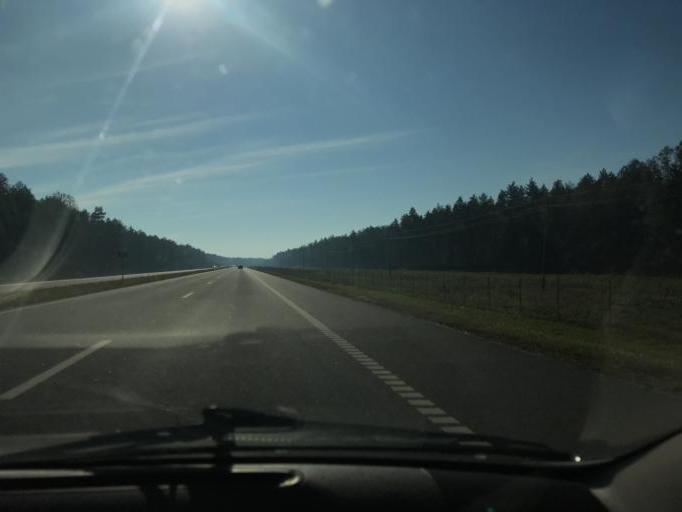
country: BY
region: Minsk
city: Slutsk
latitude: 53.2995
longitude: 27.5440
